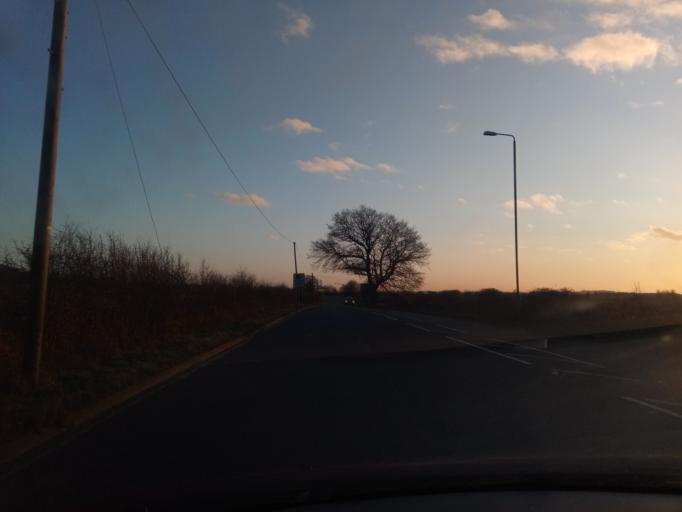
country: GB
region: England
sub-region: Nottinghamshire
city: Farnsfield
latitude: 53.0887
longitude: -1.0702
